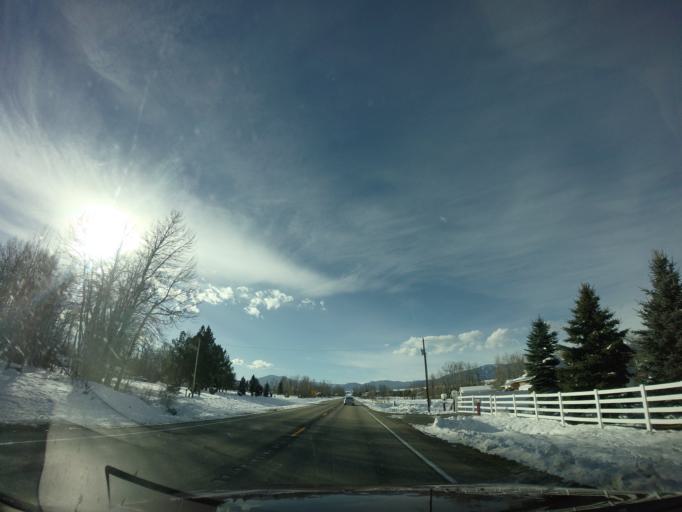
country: US
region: Montana
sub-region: Carbon County
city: Red Lodge
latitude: 45.2586
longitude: -109.2286
